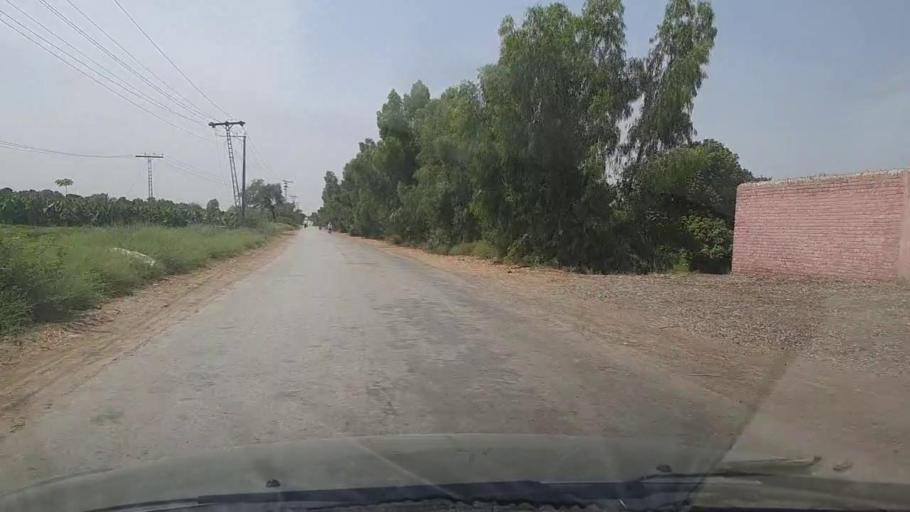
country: PK
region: Sindh
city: Bhiria
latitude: 26.9027
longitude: 68.2071
